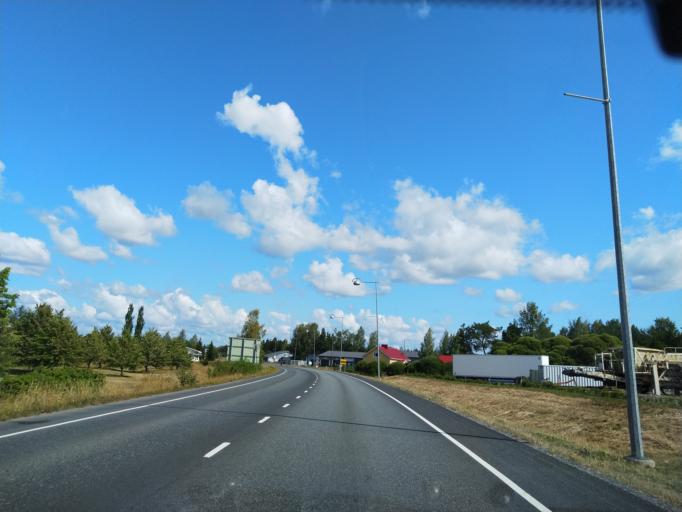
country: FI
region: Satakunta
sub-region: Pori
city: Huittinen
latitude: 61.1673
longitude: 22.7072
